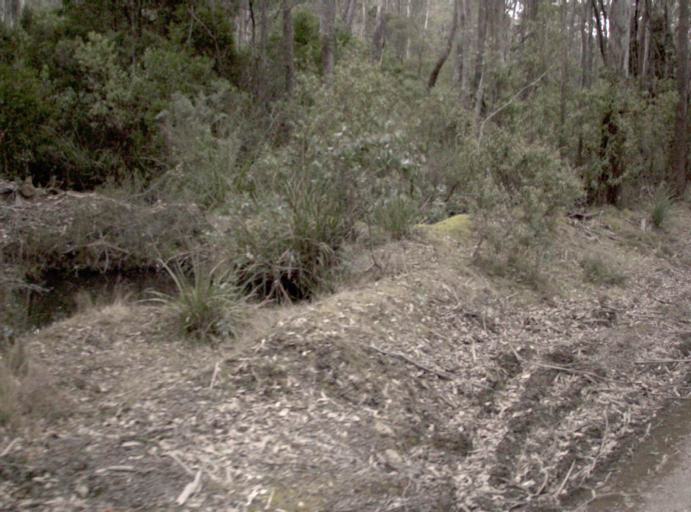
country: AU
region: Tasmania
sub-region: Launceston
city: Newstead
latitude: -41.3546
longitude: 147.2228
